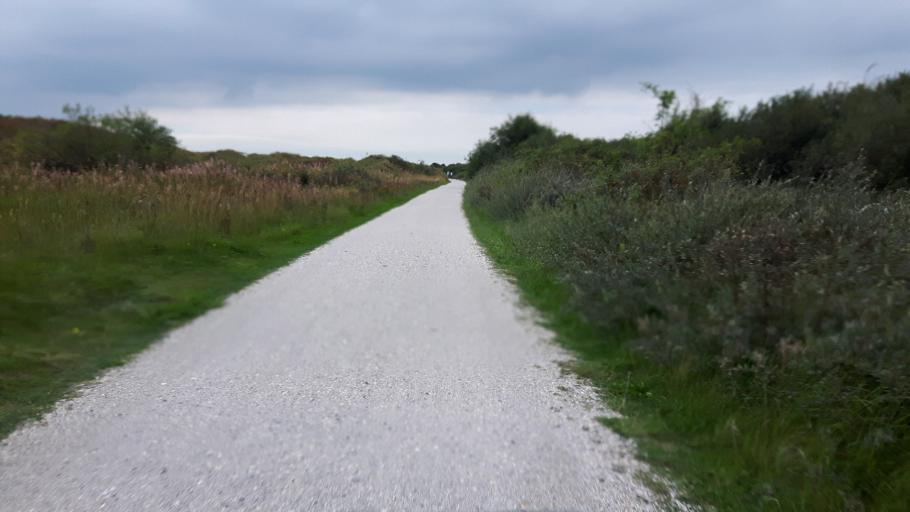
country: NL
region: Friesland
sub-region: Gemeente Dongeradeel
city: Holwerd
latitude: 53.4613
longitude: 5.8924
